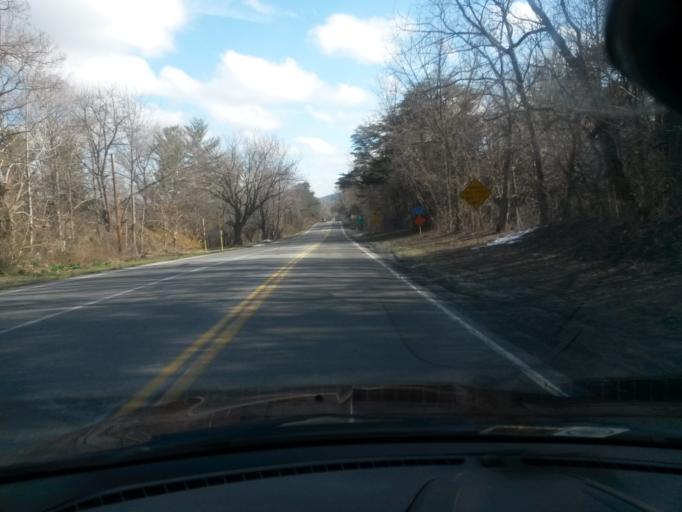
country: US
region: Virginia
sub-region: Augusta County
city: Jolivue
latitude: 38.0790
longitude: -79.0992
